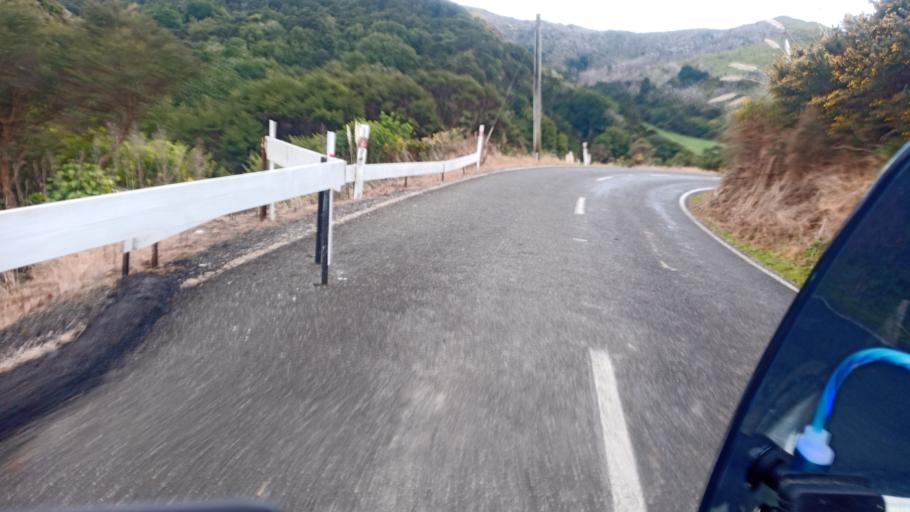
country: NZ
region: Gisborne
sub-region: Gisborne District
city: Gisborne
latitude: -38.3182
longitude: 178.3162
